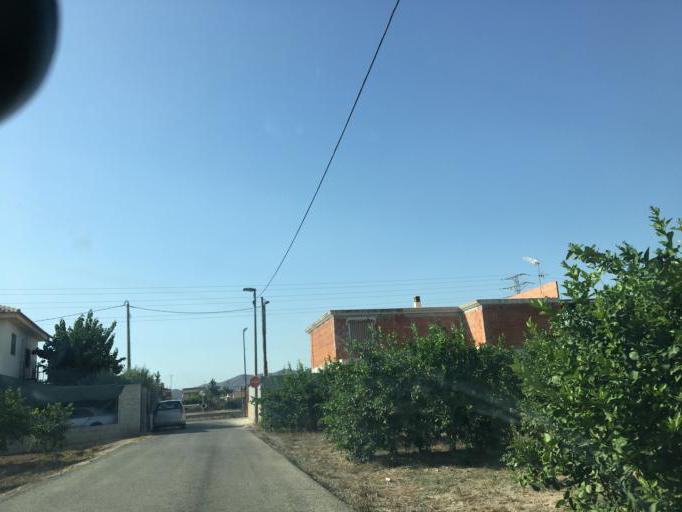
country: ES
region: Murcia
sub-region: Murcia
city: Santomera
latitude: 38.0318
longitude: -1.0581
